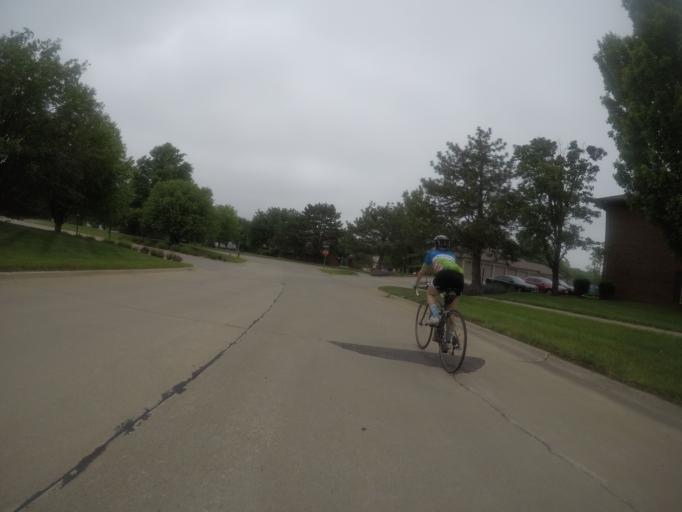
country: US
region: Kansas
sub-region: Riley County
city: Manhattan
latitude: 39.1947
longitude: -96.6038
